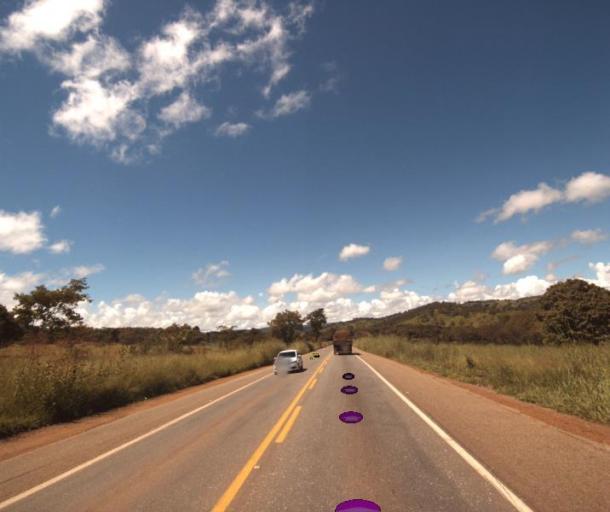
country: BR
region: Goias
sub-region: Pirenopolis
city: Pirenopolis
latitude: -16.0726
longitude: -49.0562
